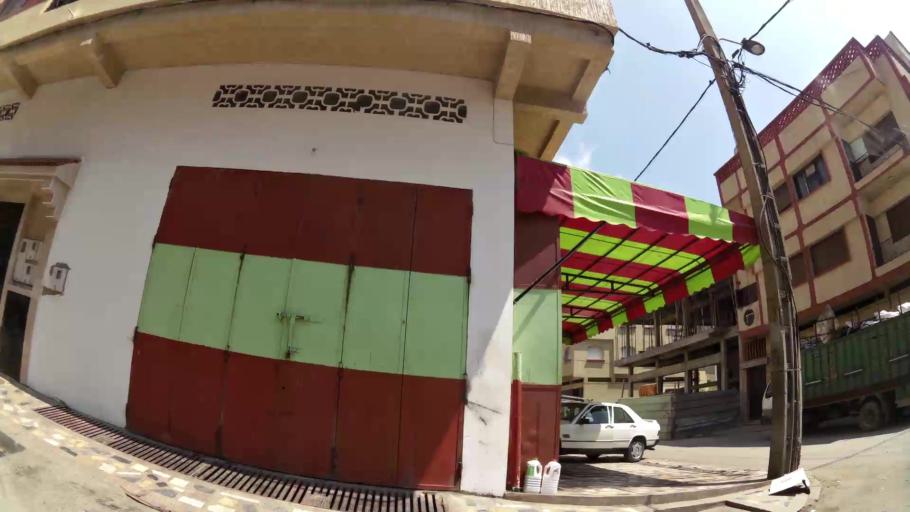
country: MA
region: Rabat-Sale-Zemmour-Zaer
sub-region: Skhirate-Temara
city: Temara
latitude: 33.9706
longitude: -6.8885
